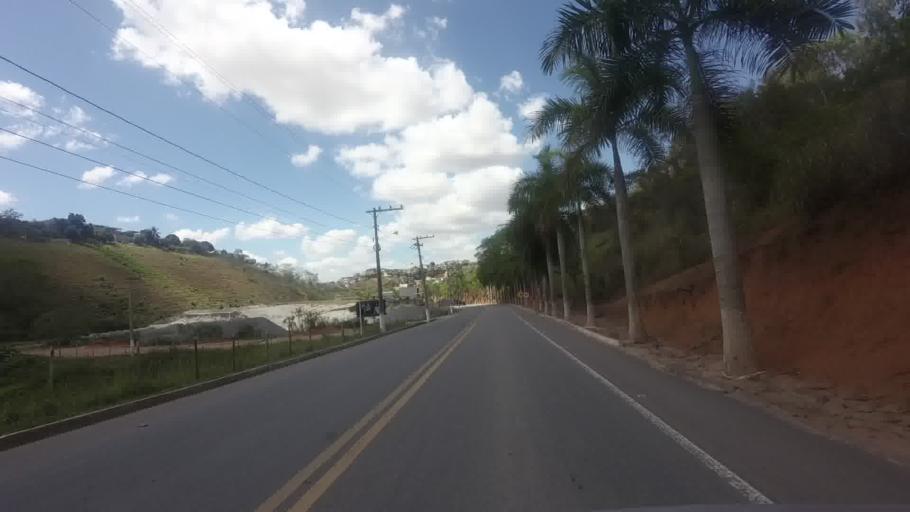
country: BR
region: Minas Gerais
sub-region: Recreio
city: Recreio
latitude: -21.6555
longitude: -42.3555
